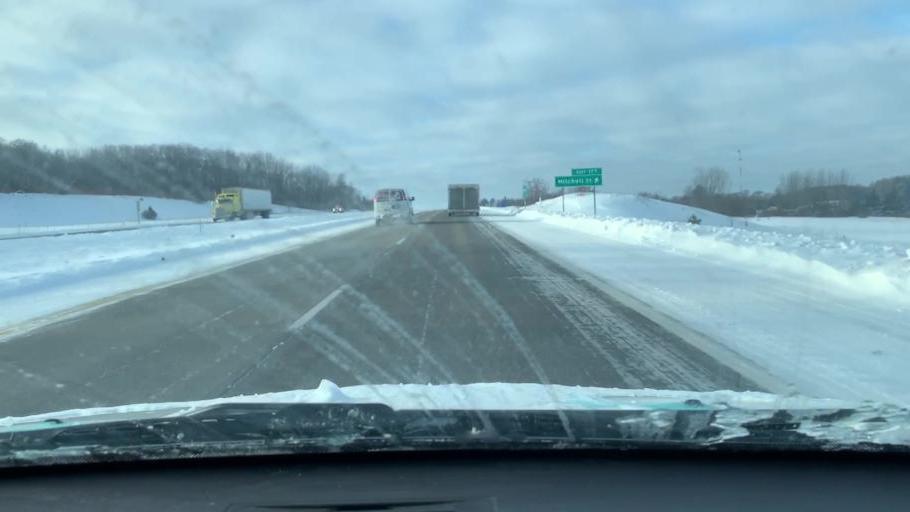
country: US
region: Michigan
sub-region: Wexford County
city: Cadillac
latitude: 44.2259
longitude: -85.3876
